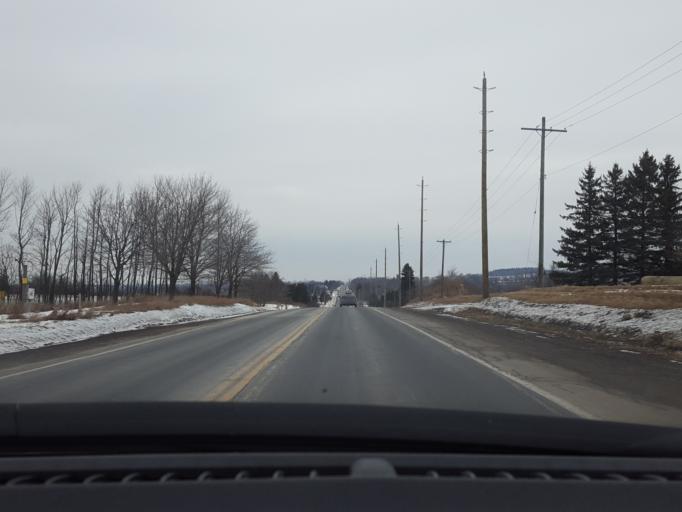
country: CA
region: Ontario
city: Keswick
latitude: 44.1504
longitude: -79.4276
